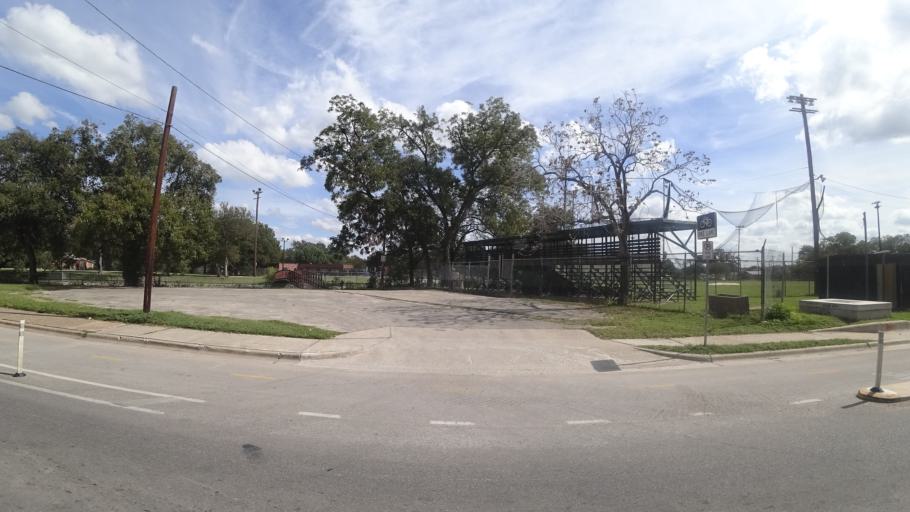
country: US
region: Texas
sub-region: Travis County
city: Austin
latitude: 30.2628
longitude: -97.7129
